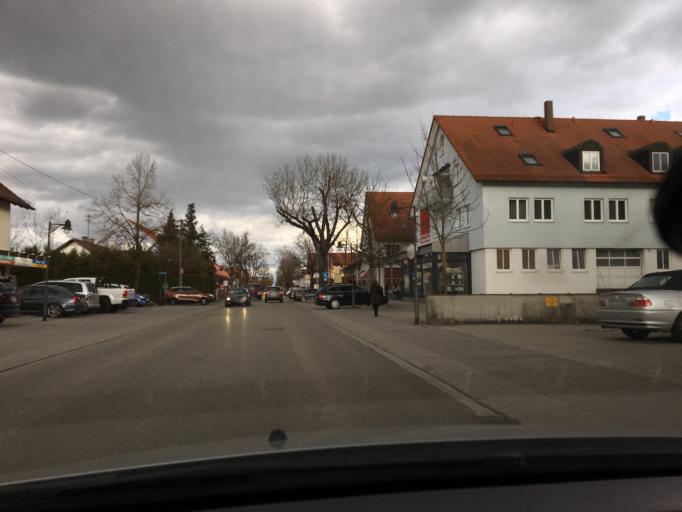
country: DE
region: Bavaria
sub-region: Upper Bavaria
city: Hallbergmoos
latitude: 48.3195
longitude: 11.7463
